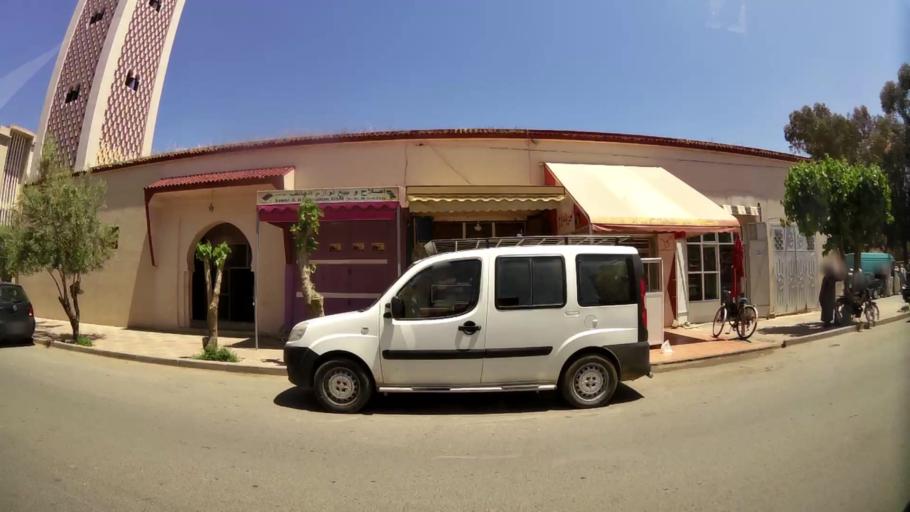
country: MA
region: Oriental
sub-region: Oujda-Angad
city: Oujda
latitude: 34.6708
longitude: -1.9386
